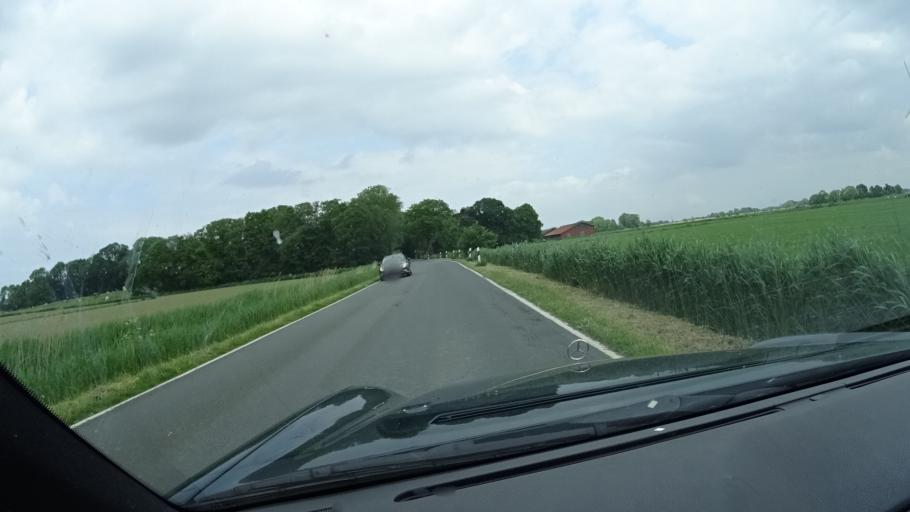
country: DE
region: Lower Saxony
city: Butjadingen
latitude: 53.5967
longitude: 8.2845
